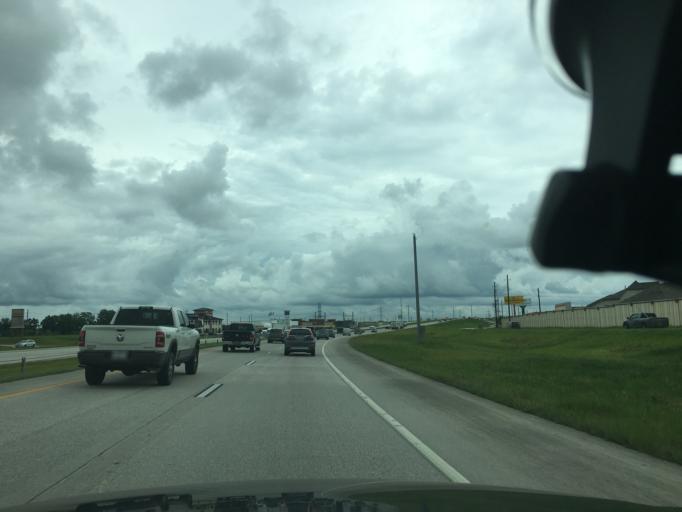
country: US
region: Texas
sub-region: Harris County
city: Tomball
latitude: 30.0846
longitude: -95.5353
